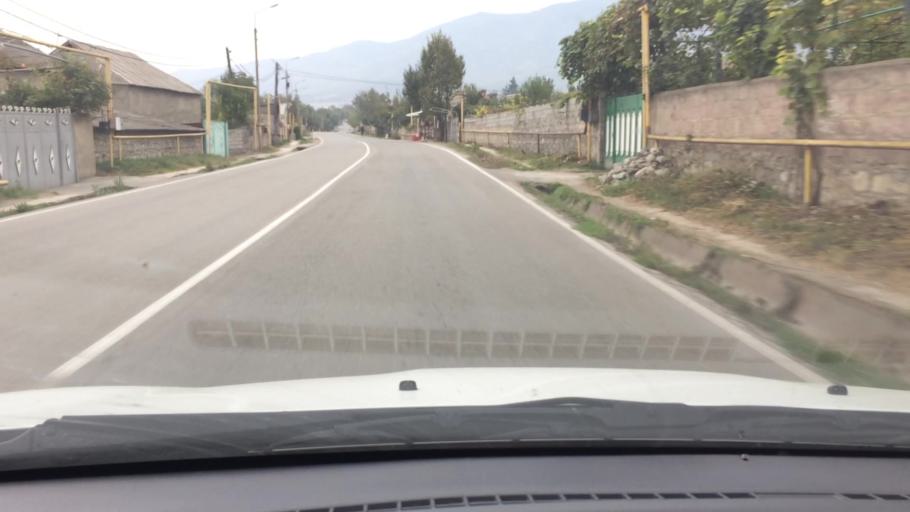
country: AM
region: Tavush
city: Bagratashen
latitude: 41.2419
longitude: 44.7992
